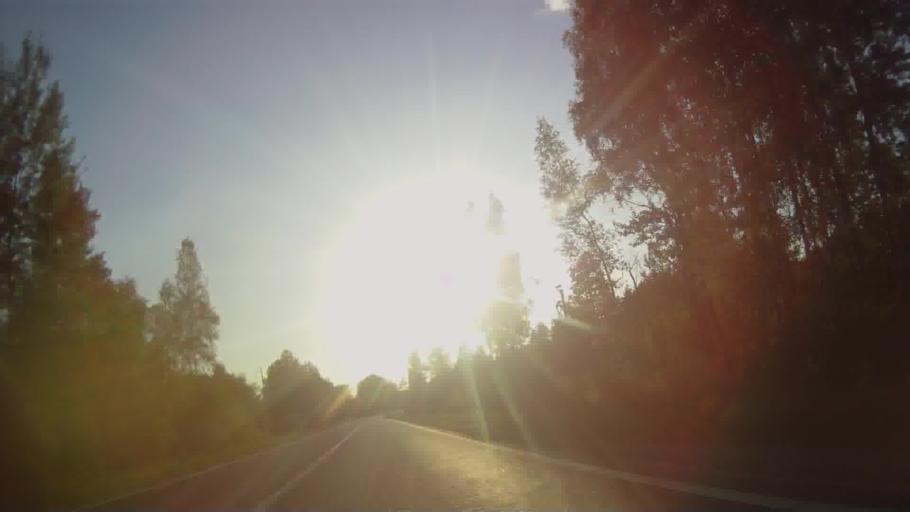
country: LV
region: Livani
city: Livani
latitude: 56.5290
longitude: 26.1494
